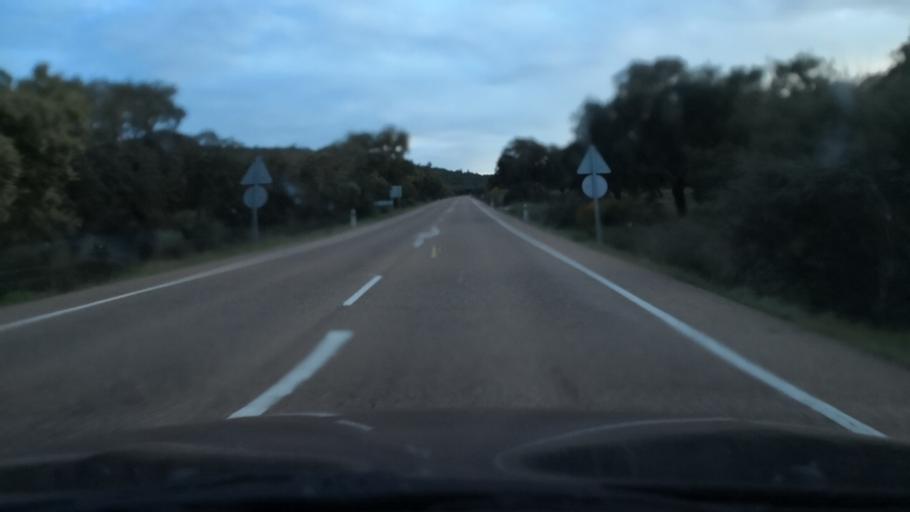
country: ES
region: Extremadura
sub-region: Provincia de Badajoz
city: Puebla de Obando
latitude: 39.1956
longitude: -6.5946
